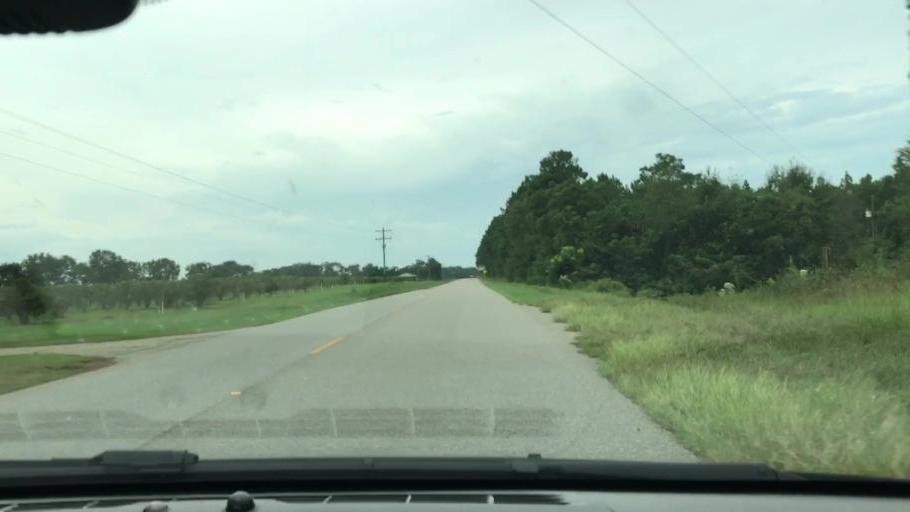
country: US
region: Alabama
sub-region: Houston County
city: Ashford
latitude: 31.2606
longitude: -85.1667
